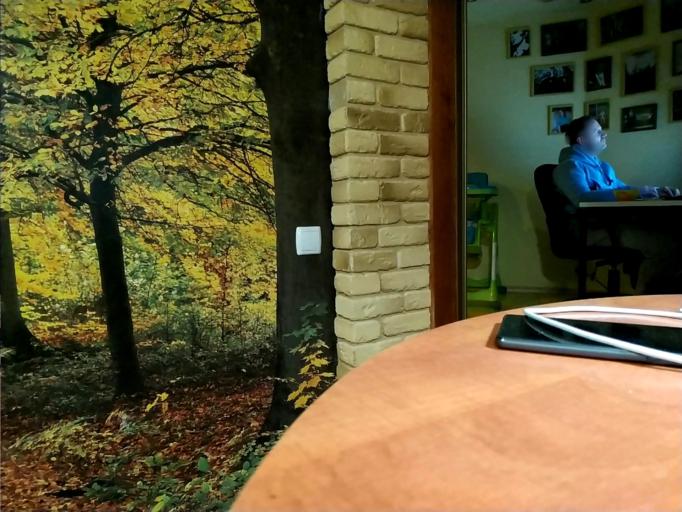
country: BY
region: Minsk
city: Plyeshchanitsy
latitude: 54.4280
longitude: 27.6240
